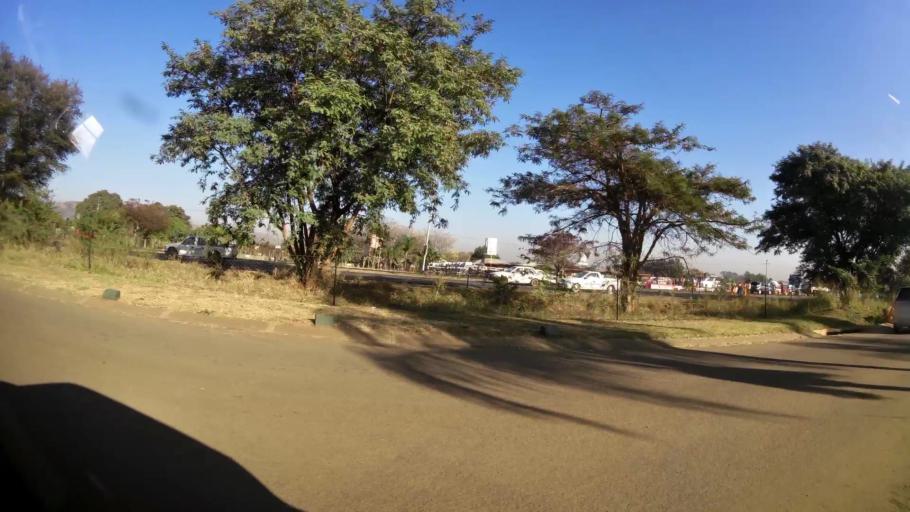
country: ZA
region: Gauteng
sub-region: City of Tshwane Metropolitan Municipality
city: Pretoria
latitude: -25.6673
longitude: 28.1934
